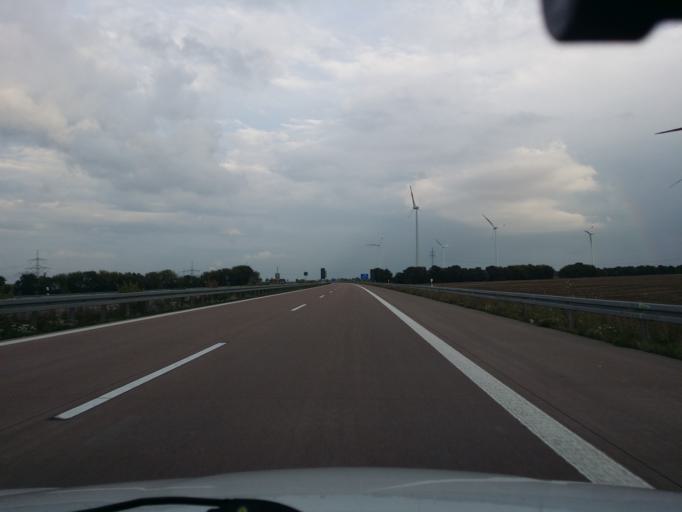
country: DE
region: Saxony-Anhalt
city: Obhausen
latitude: 51.4020
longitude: 11.7103
